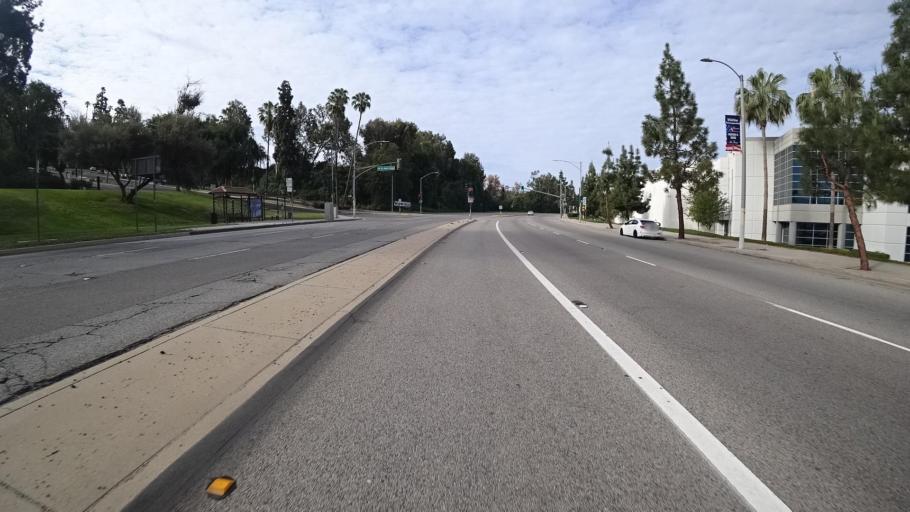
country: US
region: California
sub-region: Los Angeles County
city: South El Monte
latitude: 34.0205
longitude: -118.0376
